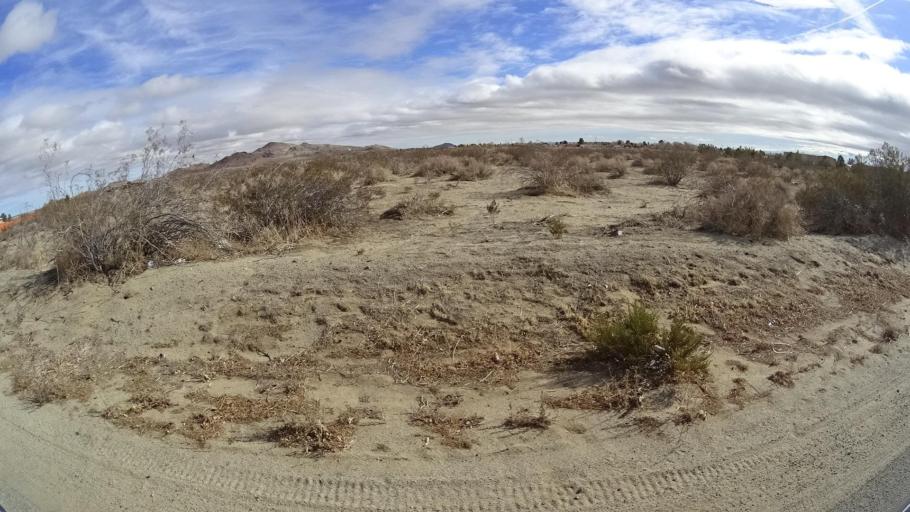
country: US
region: California
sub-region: Kern County
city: Rosamond
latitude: 34.8698
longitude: -118.2203
